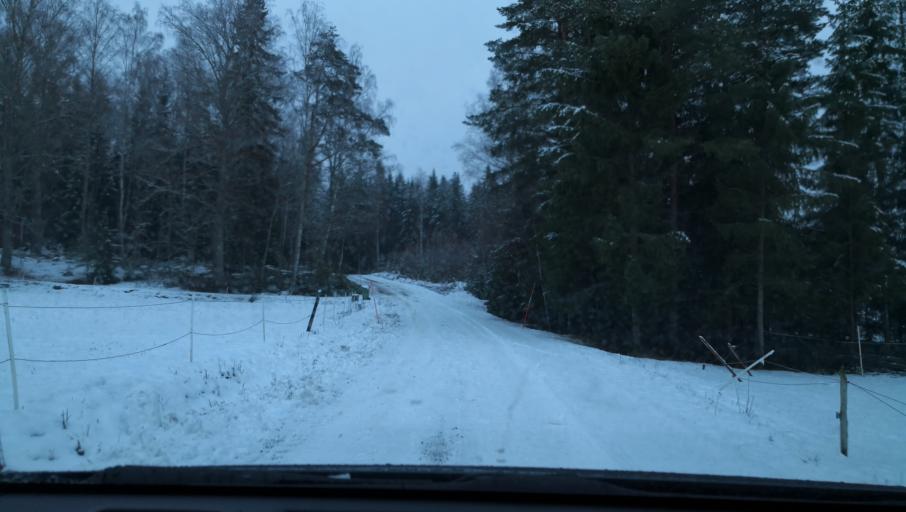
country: SE
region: Vaestmanland
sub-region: Kopings Kommun
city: Kolsva
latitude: 59.5603
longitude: 15.8413
